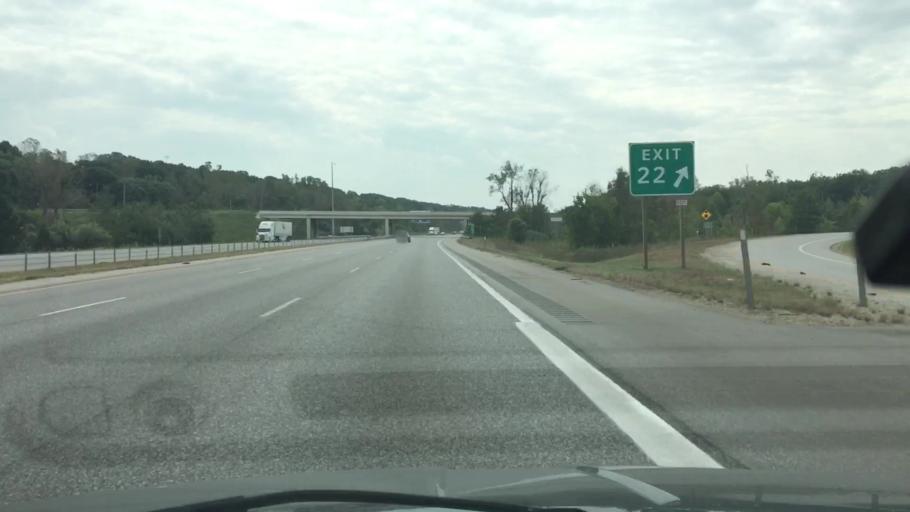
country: US
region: Michigan
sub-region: Berrien County
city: Stevensville
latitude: 42.0128
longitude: -86.5328
